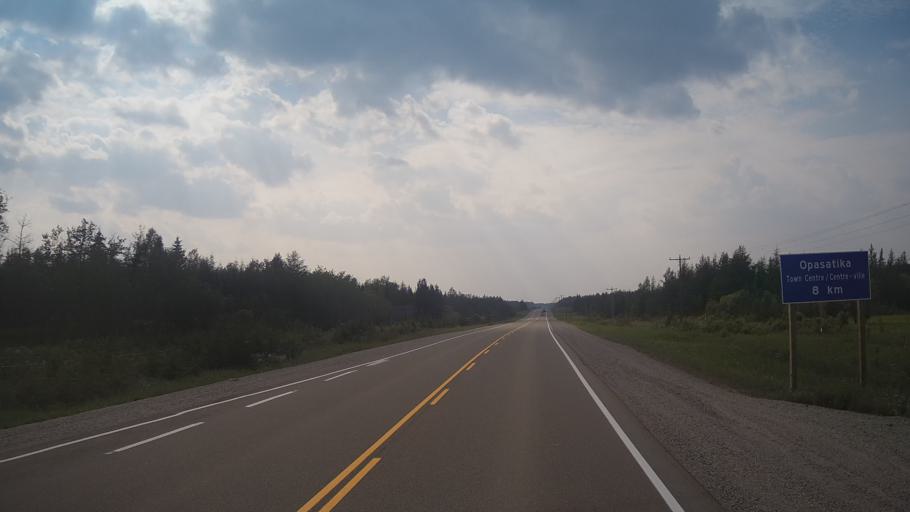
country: CA
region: Ontario
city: Kapuskasing
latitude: 49.5081
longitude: -82.7627
